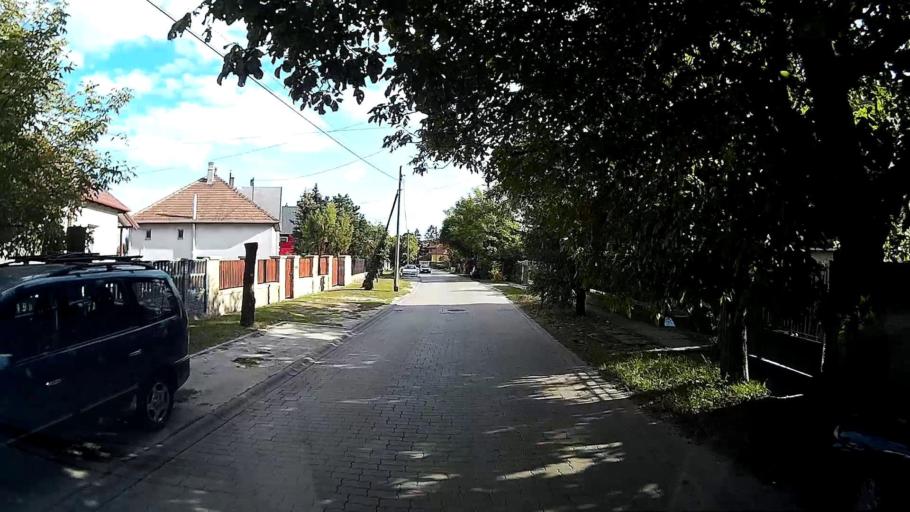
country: HU
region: Pest
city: Pilisvorosvar
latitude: 47.6262
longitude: 18.9002
